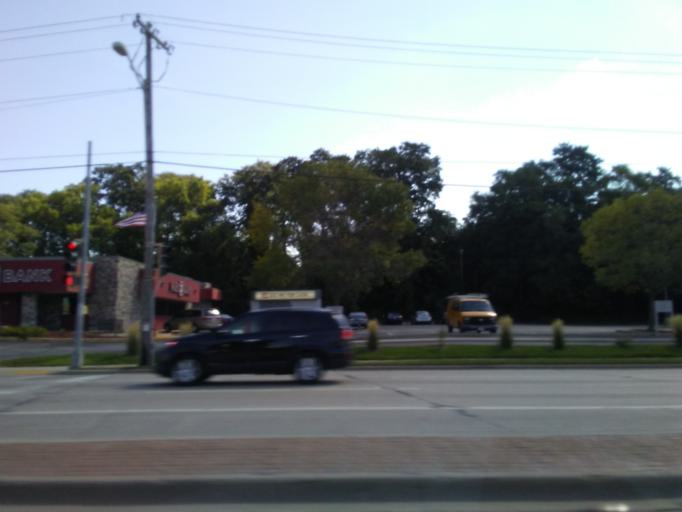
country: US
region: Wisconsin
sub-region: Dane County
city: Madison
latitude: 43.0396
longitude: -89.3941
